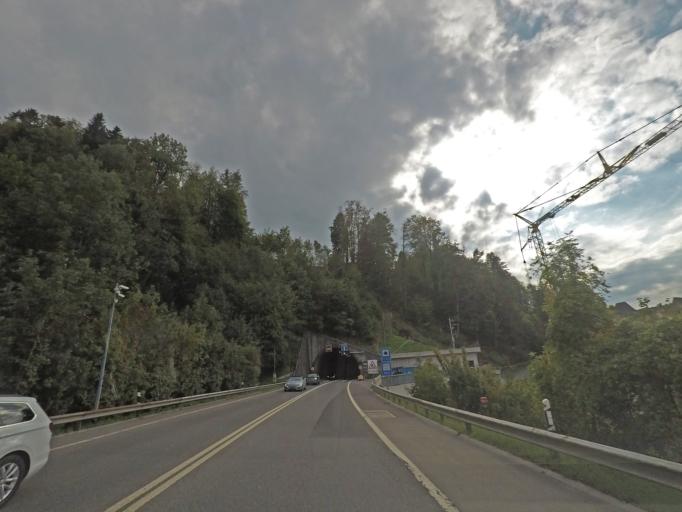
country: CH
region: Schwyz
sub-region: Bezirk Schwyz
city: Ingenbohl
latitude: 46.9978
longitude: 8.6215
